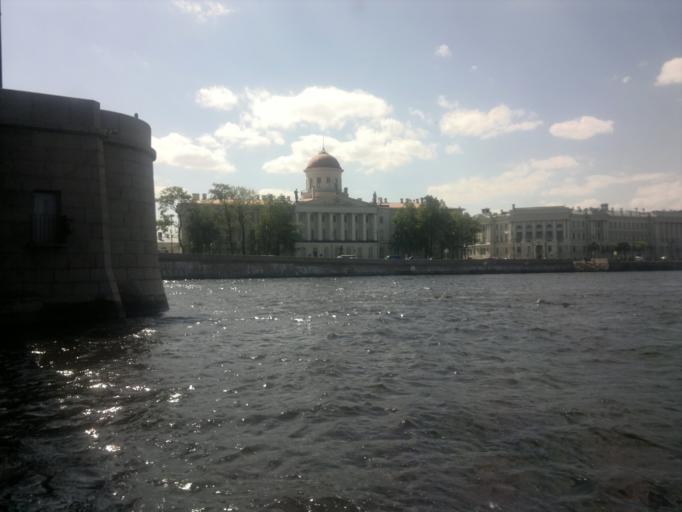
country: RU
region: St.-Petersburg
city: Saint Petersburg
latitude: 59.9462
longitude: 30.3030
